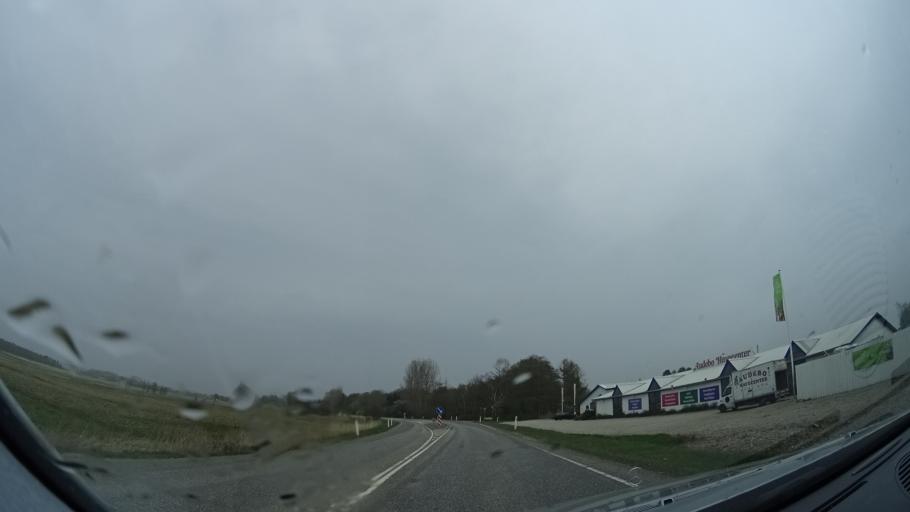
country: DK
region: Zealand
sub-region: Holbaek Kommune
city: Holbaek
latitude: 55.7587
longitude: 11.6280
